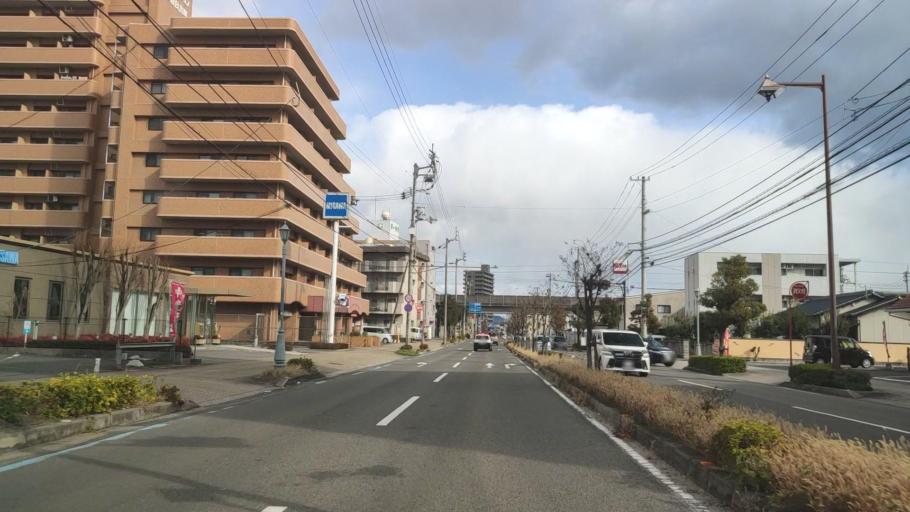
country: JP
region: Ehime
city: Hojo
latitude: 34.0657
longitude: 132.9902
